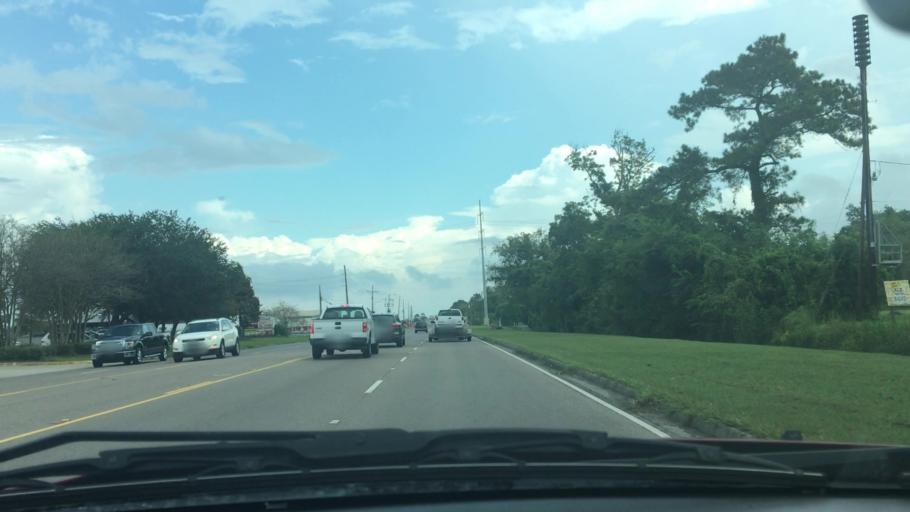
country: US
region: Louisiana
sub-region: Saint John the Baptist Parish
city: Laplace
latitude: 30.0679
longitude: -90.4804
